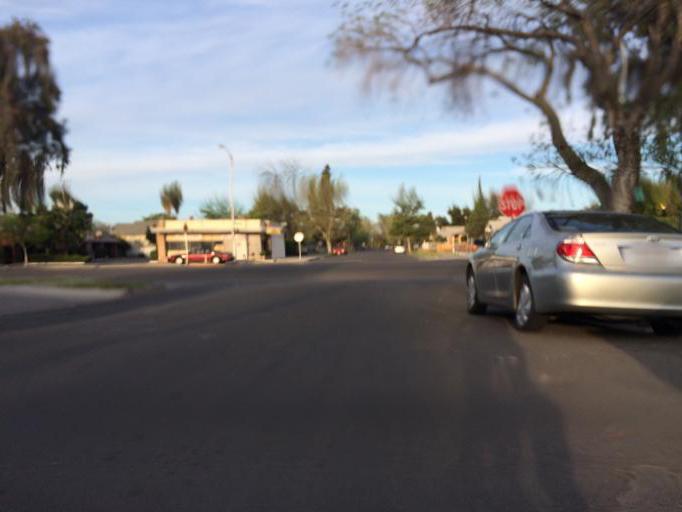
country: US
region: California
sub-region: Fresno County
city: Fresno
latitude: 36.7450
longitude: -119.7720
